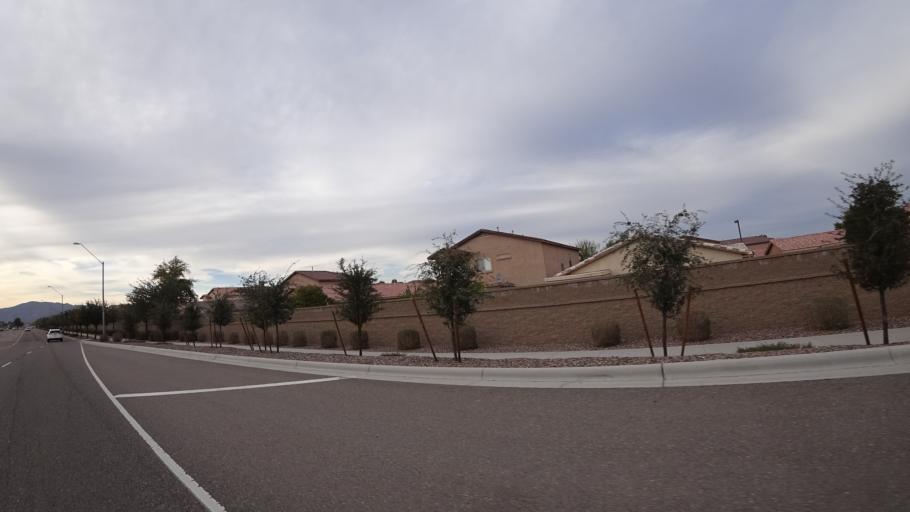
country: US
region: Arizona
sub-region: Maricopa County
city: Citrus Park
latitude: 33.6242
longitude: -112.4209
